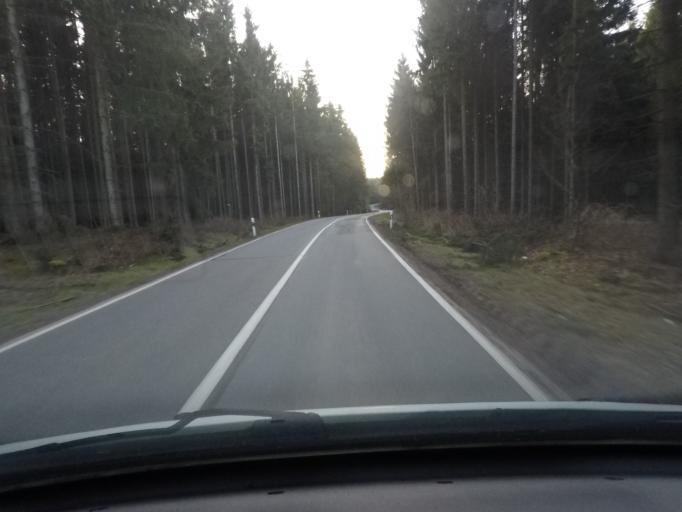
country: DE
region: Saxony
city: Dippoldiswalde
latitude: 50.8965
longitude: 13.6241
